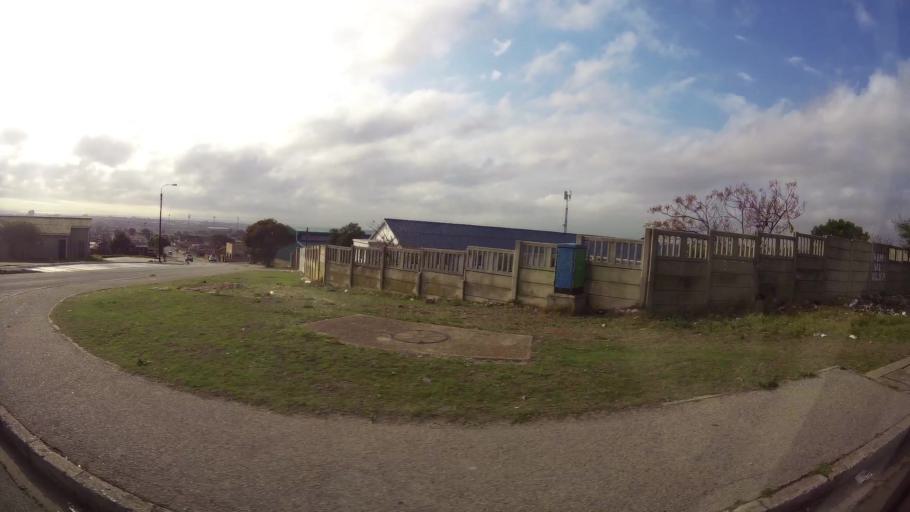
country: ZA
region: Eastern Cape
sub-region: Nelson Mandela Bay Metropolitan Municipality
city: Port Elizabeth
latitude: -33.9170
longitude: 25.5495
